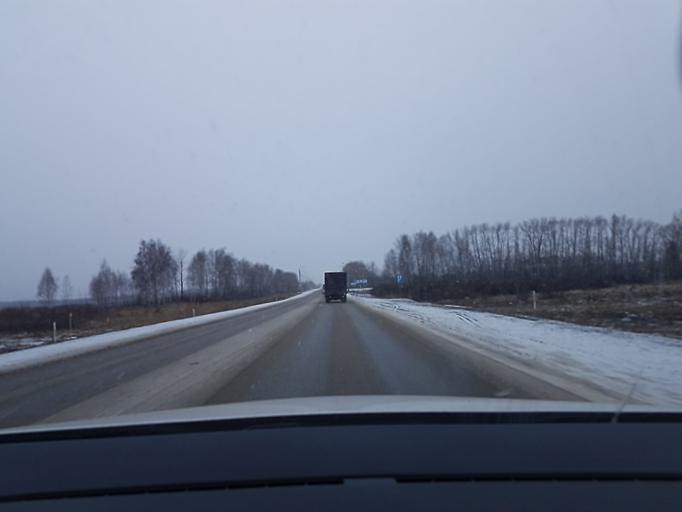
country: RU
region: Tambov
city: Pervomayskiy
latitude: 53.2433
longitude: 40.2567
